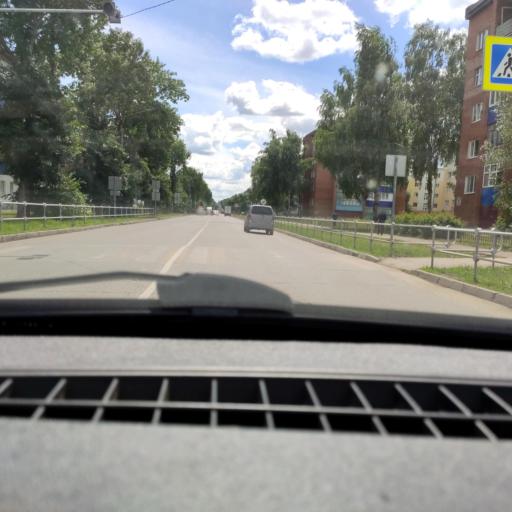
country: RU
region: Bashkortostan
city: Sterlitamak
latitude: 53.6411
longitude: 55.9323
